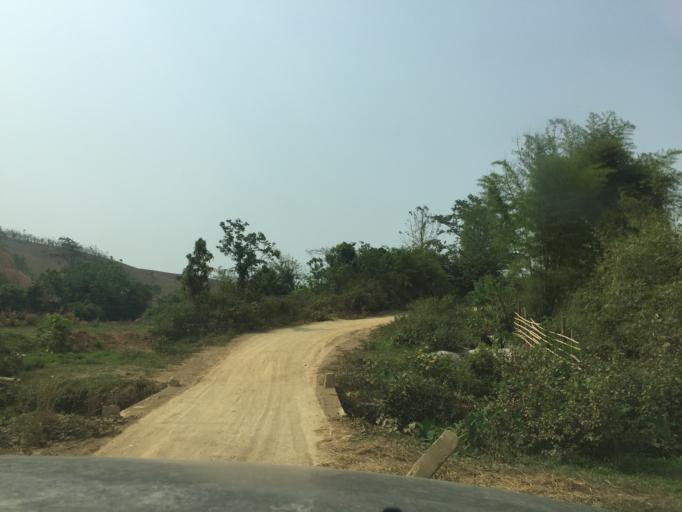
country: TH
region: Uttaradit
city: Ban Khok
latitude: 17.9471
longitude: 101.2829
